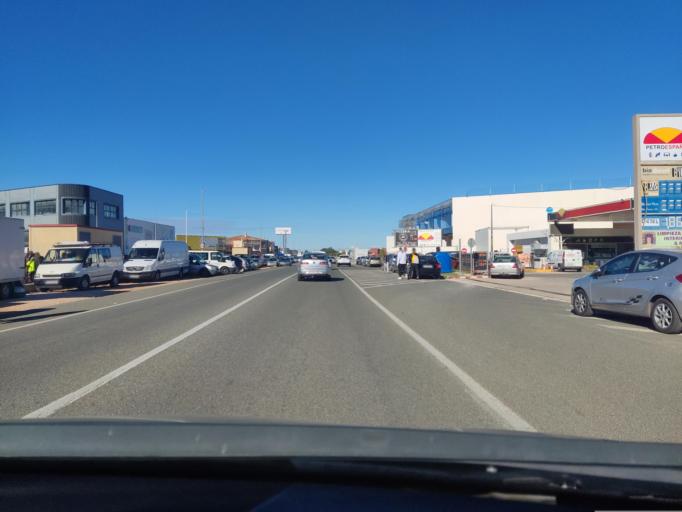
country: ES
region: Valencia
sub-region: Provincia de Alicante
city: Vergel
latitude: 38.8547
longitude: 0.0004
